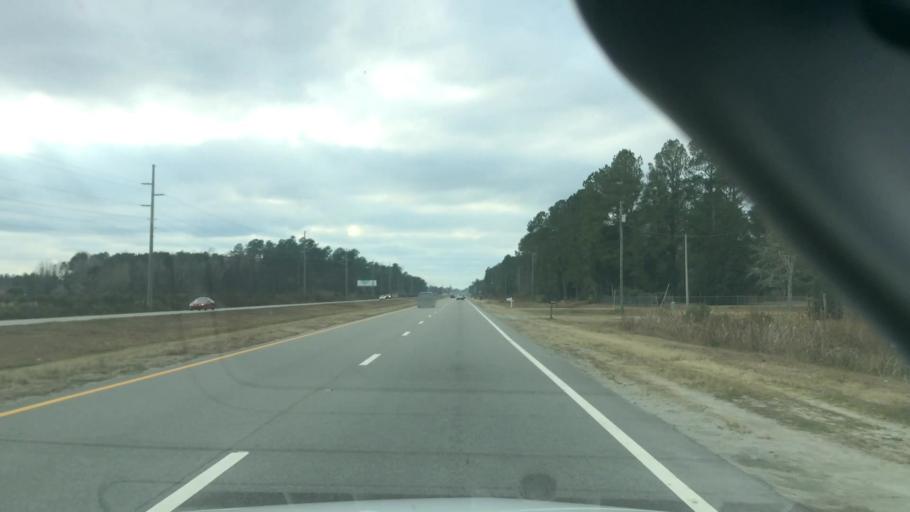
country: US
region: North Carolina
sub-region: Brunswick County
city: Sunset Beach
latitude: 33.9426
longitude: -78.5284
